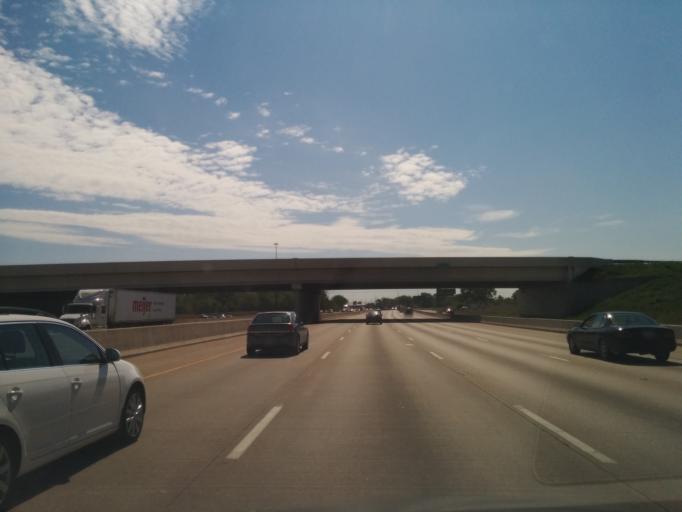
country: US
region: Indiana
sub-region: Lake County
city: Gary
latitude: 41.5691
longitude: -87.3571
